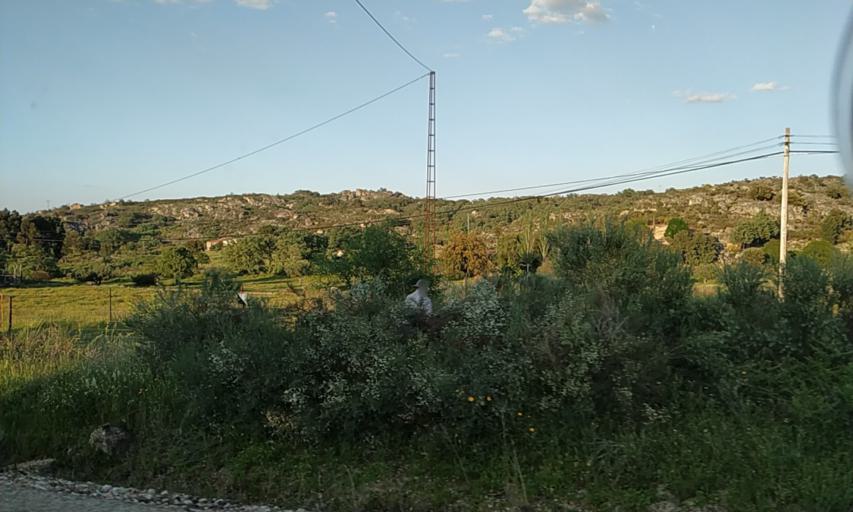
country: PT
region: Portalegre
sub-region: Portalegre
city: Sao Juliao
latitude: 39.3580
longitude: -7.2752
